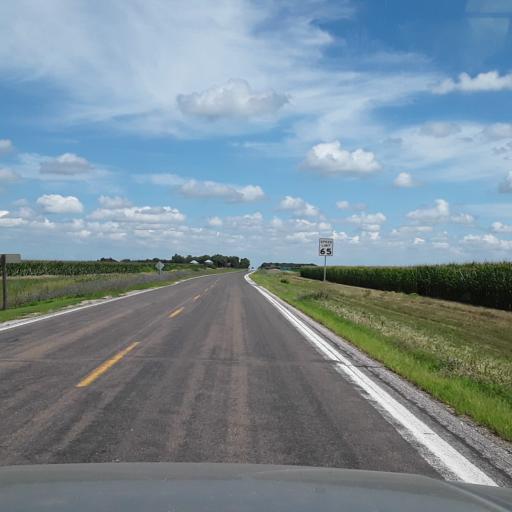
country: US
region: Nebraska
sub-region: Polk County
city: Osceola
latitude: 41.0325
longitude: -97.4063
